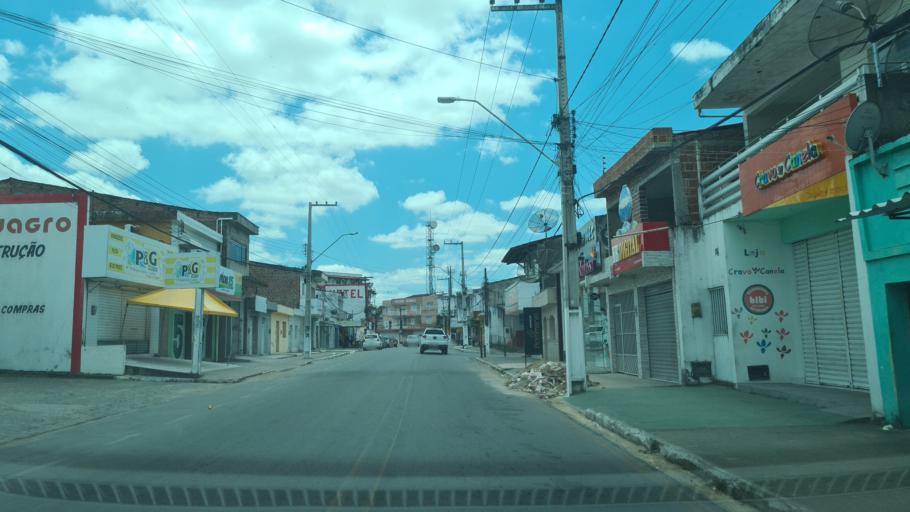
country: BR
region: Alagoas
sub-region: Uniao Dos Palmares
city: Uniao dos Palmares
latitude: -9.1603
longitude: -36.0300
